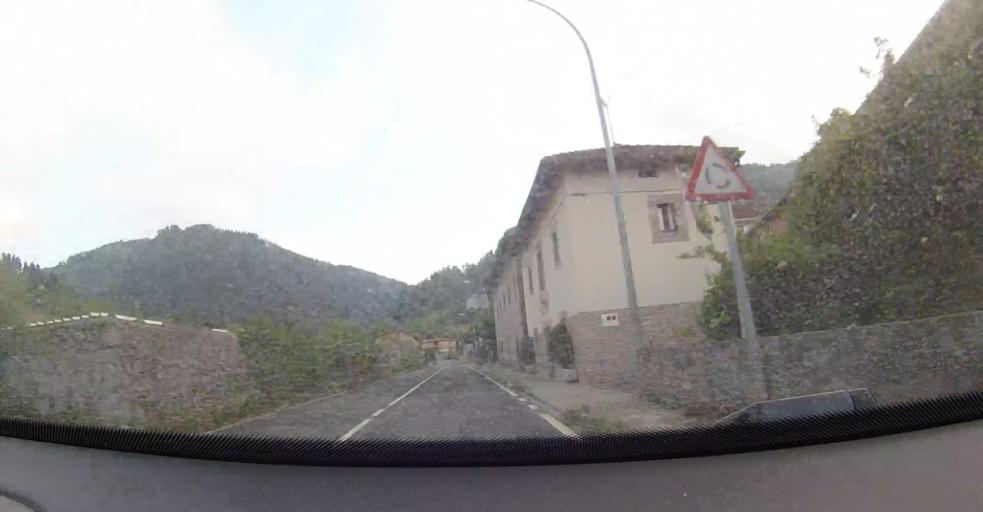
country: ES
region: Basque Country
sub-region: Bizkaia
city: Sopuerta
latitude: 43.2511
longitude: -3.1553
